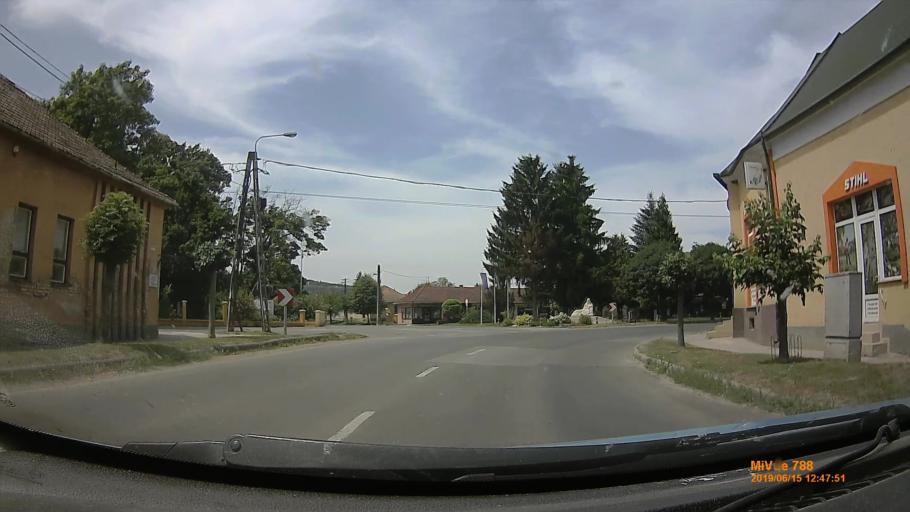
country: HU
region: Baranya
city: Sasd
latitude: 46.2528
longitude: 18.1068
